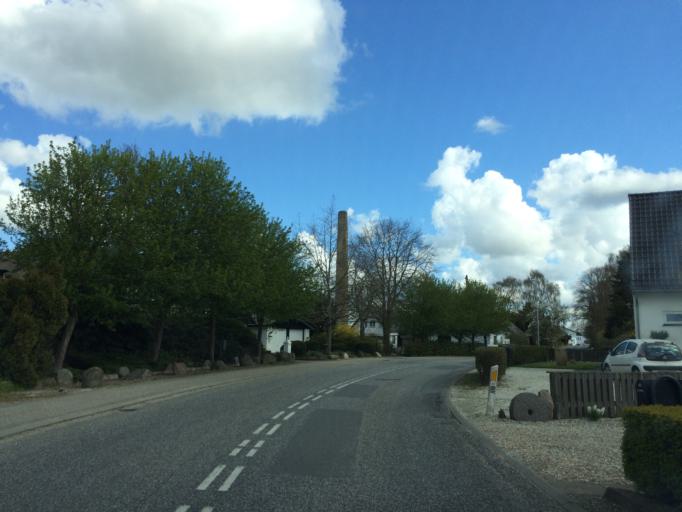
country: DK
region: South Denmark
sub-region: Odense Kommune
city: Bellinge
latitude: 55.2696
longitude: 10.3058
